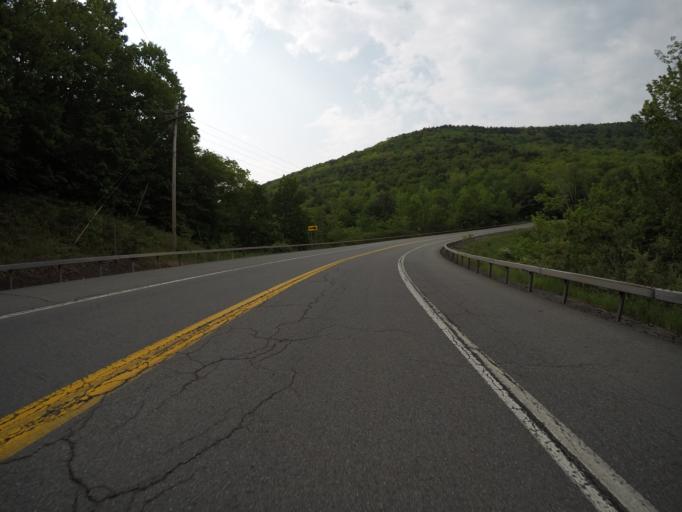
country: US
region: New York
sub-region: Sullivan County
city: Livingston Manor
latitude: 42.0726
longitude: -74.8310
